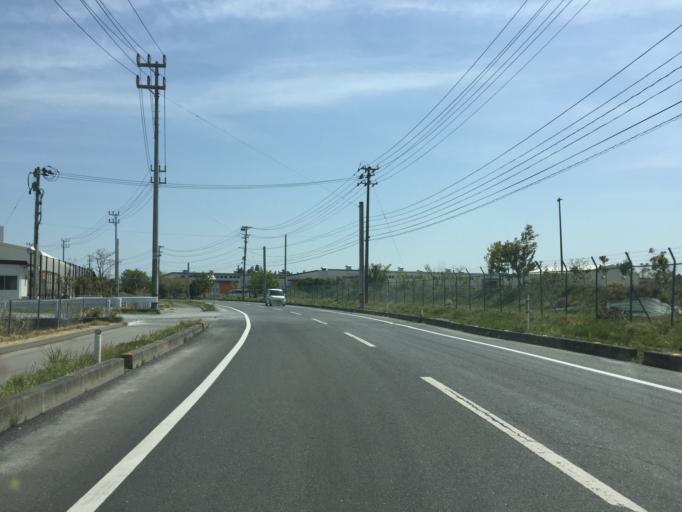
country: JP
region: Miyagi
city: Marumori
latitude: 37.8284
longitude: 140.9469
